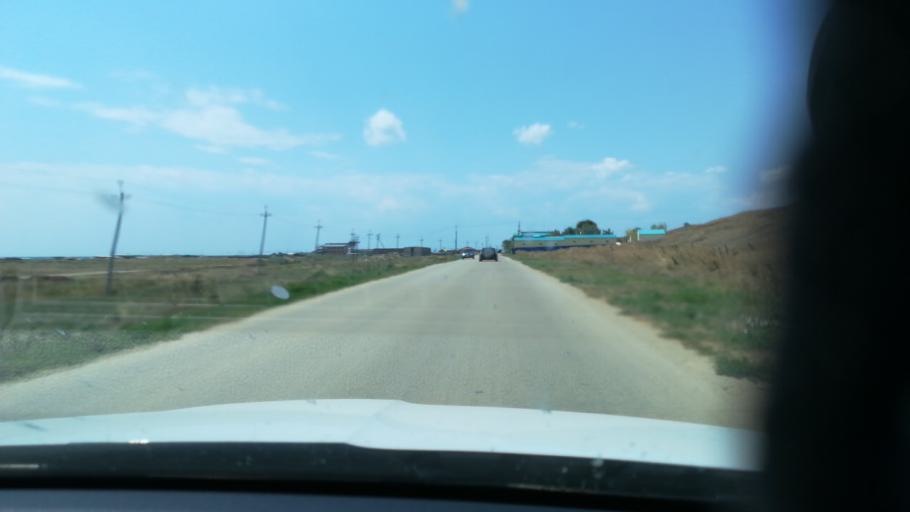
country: RU
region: Krasnodarskiy
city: Vyshestebliyevskaya
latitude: 45.1148
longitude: 36.8889
